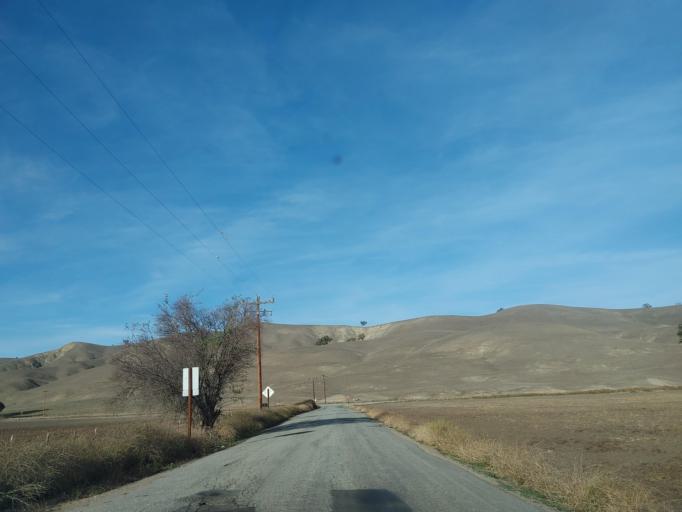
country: US
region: California
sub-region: San Benito County
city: Ridgemark
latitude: 36.7059
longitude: -121.3286
